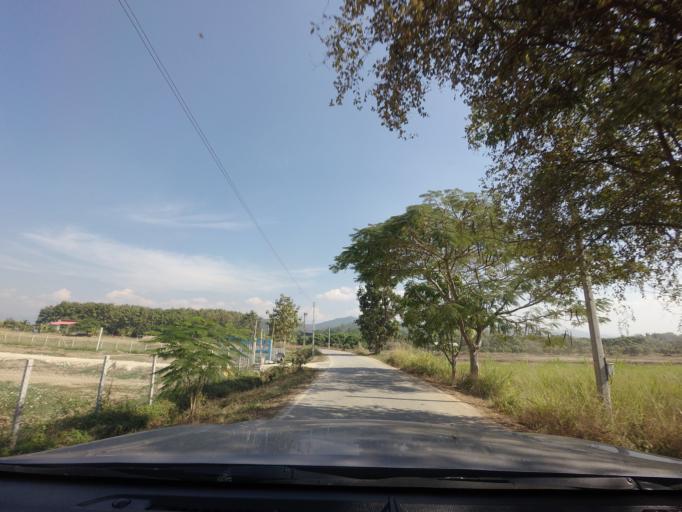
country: TH
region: Chiang Mai
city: San Kamphaeng
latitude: 18.7093
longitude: 99.1592
